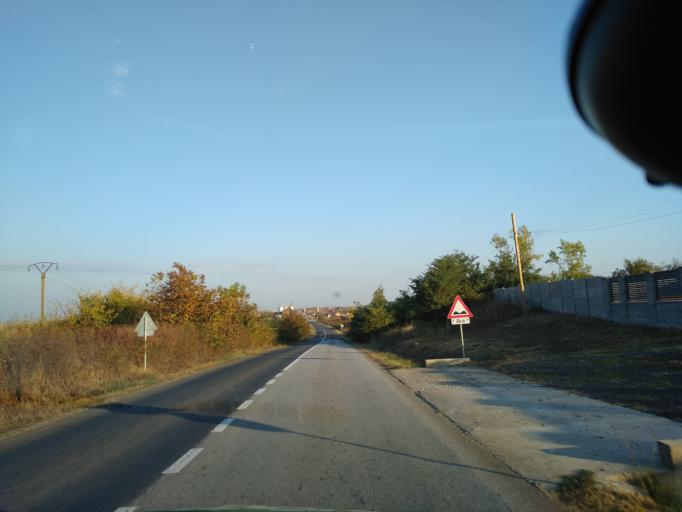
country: RO
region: Timis
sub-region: Comuna Pischia
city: Pischia
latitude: 45.8909
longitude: 21.3478
